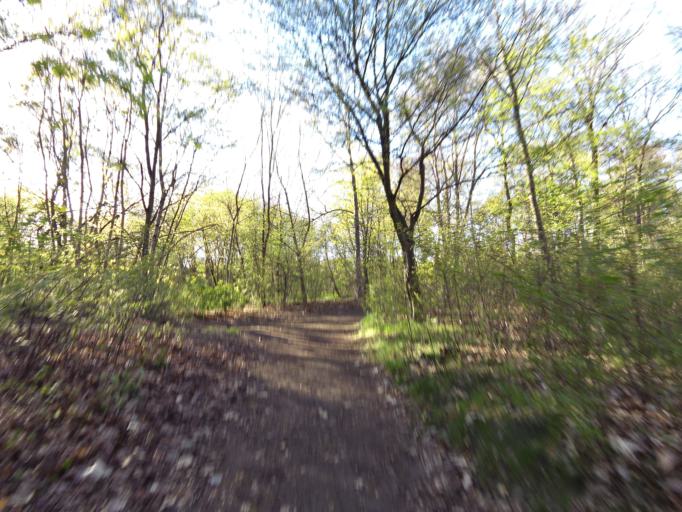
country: DE
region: Berlin
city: Oberschoneweide
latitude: 52.4697
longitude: 13.5213
